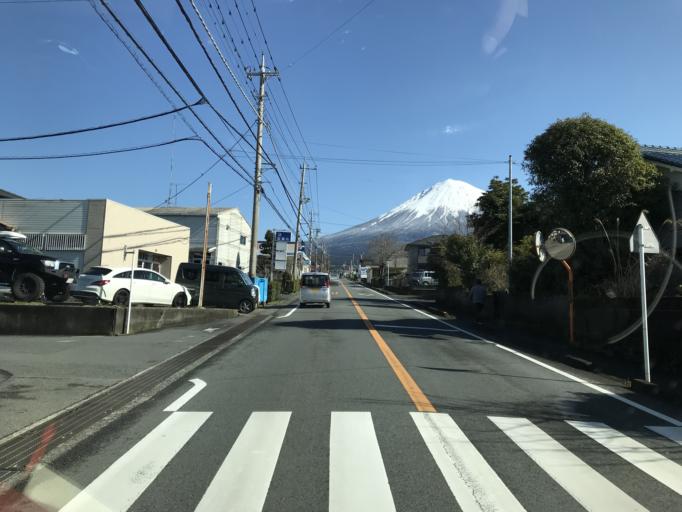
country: JP
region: Shizuoka
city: Fujinomiya
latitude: 35.2499
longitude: 138.6274
